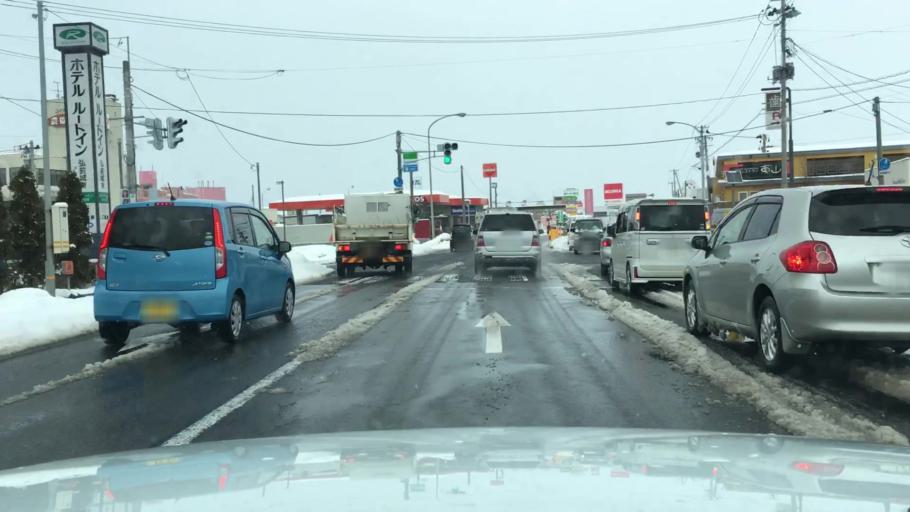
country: JP
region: Aomori
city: Hirosaki
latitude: 40.6034
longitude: 140.4993
